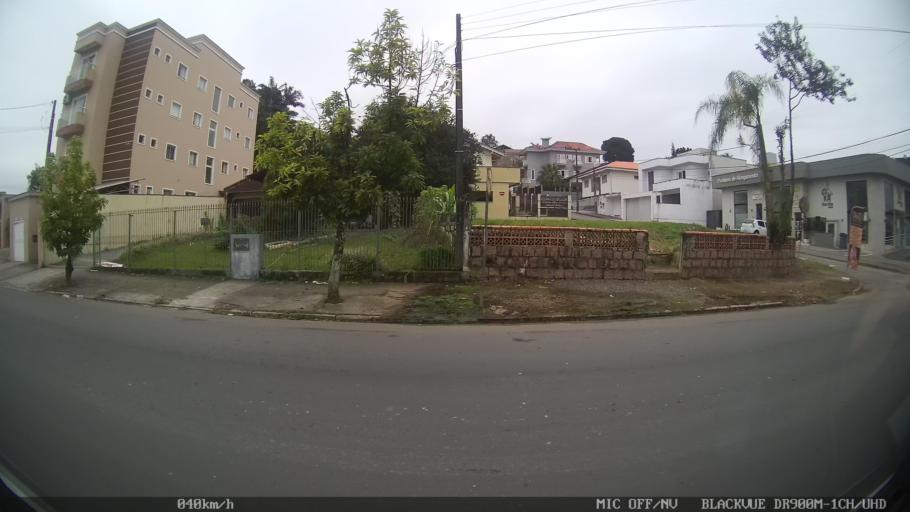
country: BR
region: Santa Catarina
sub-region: Joinville
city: Joinville
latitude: -26.2728
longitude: -48.8458
